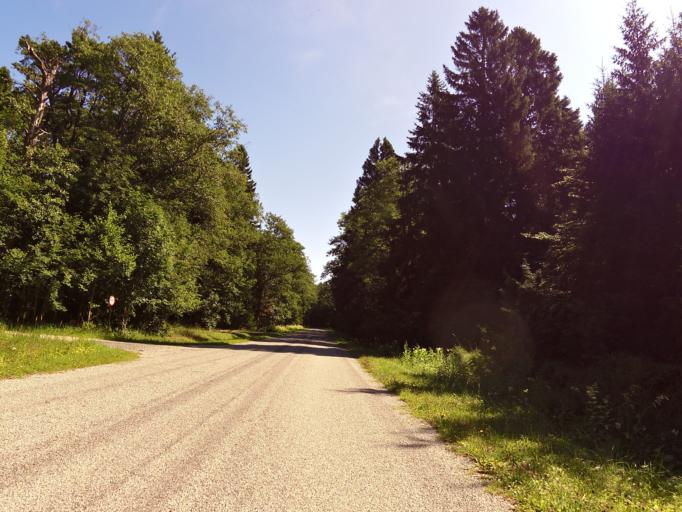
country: EE
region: Hiiumaa
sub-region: Kaerdla linn
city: Kardla
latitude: 58.9314
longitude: 22.3817
